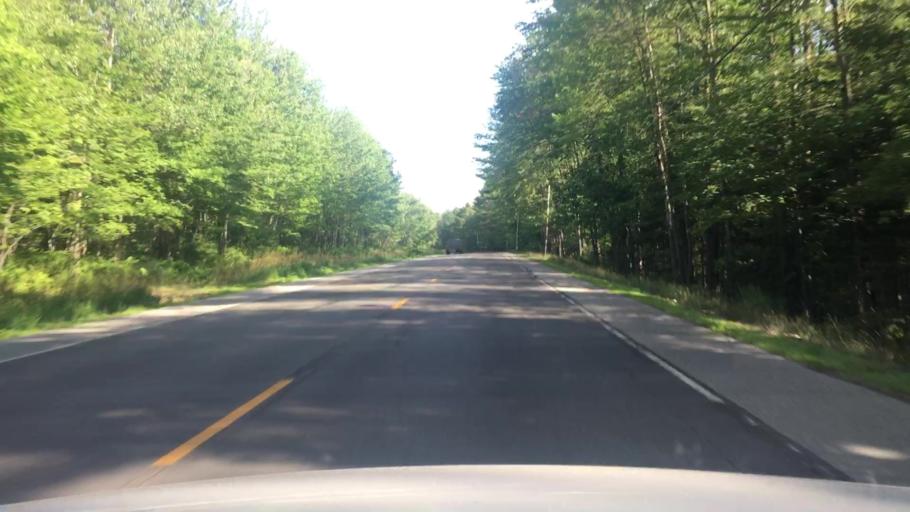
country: US
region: Maine
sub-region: Franklin County
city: Jay
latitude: 44.5346
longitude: -70.2334
